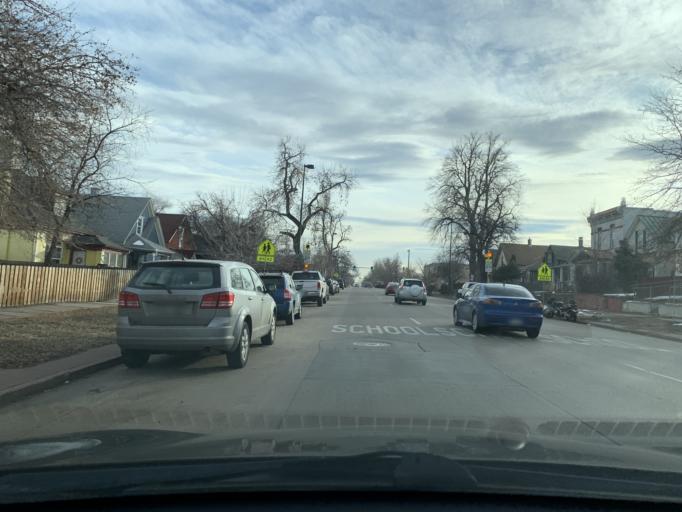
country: US
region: Colorado
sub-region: Denver County
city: Denver
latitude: 39.7366
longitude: -105.0001
